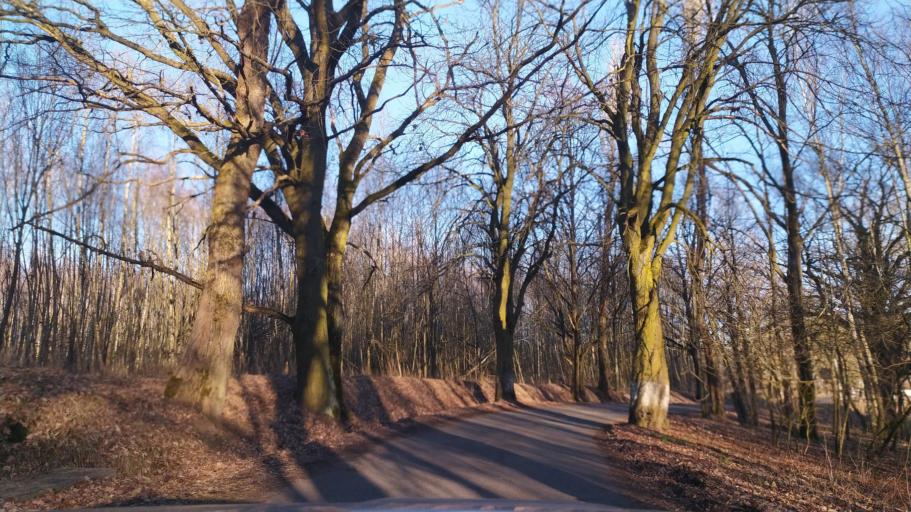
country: CZ
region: Karlovarsky
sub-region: Okres Cheb
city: Frantiskovy Lazne
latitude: 50.1146
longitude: 12.3217
